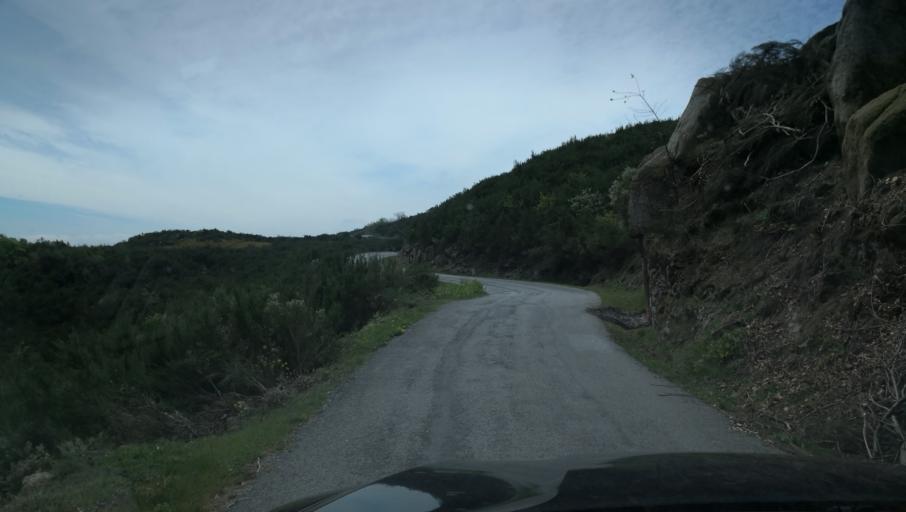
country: PT
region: Vila Real
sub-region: Vila Real
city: Vila Real
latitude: 41.3038
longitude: -7.8101
